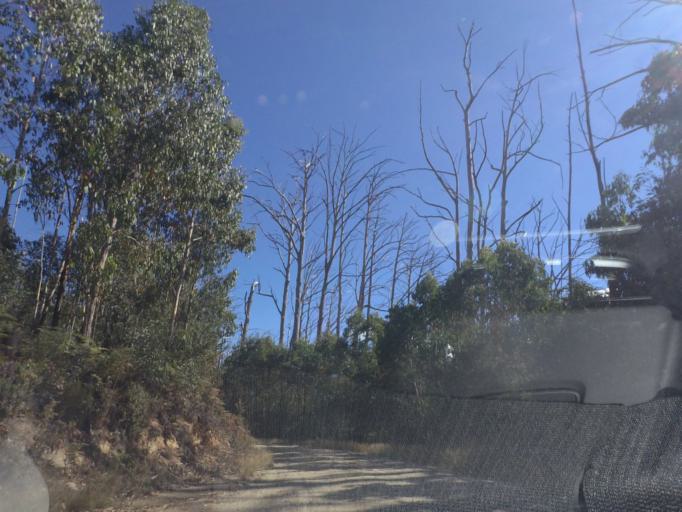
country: AU
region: Victoria
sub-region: Murrindindi
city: Alexandra
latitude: -37.4060
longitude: 145.8097
